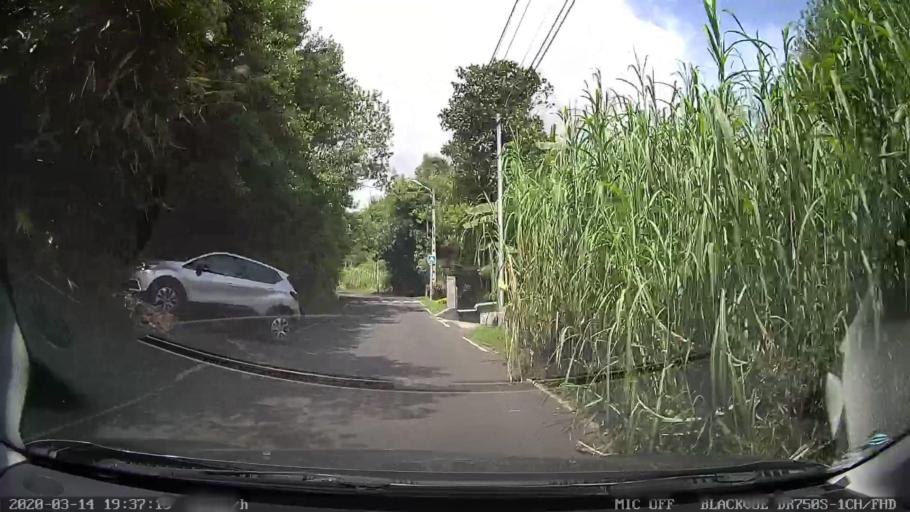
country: RE
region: Reunion
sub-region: Reunion
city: Sainte-Marie
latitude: -20.9428
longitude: 55.5226
